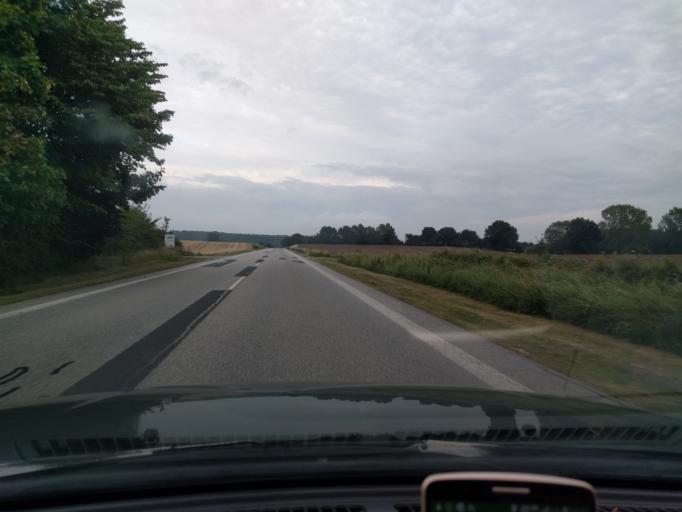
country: DK
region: Zealand
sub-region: Naestved Kommune
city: Naestved
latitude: 55.2068
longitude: 11.6510
